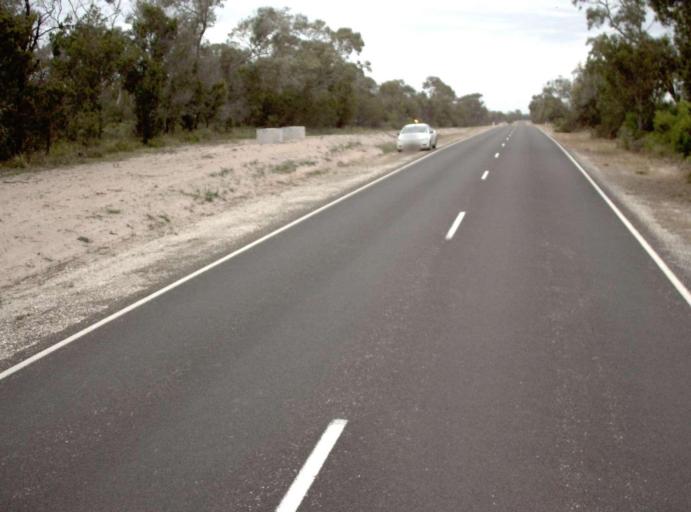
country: AU
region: Victoria
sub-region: Wellington
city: Sale
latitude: -38.1556
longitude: 147.3920
